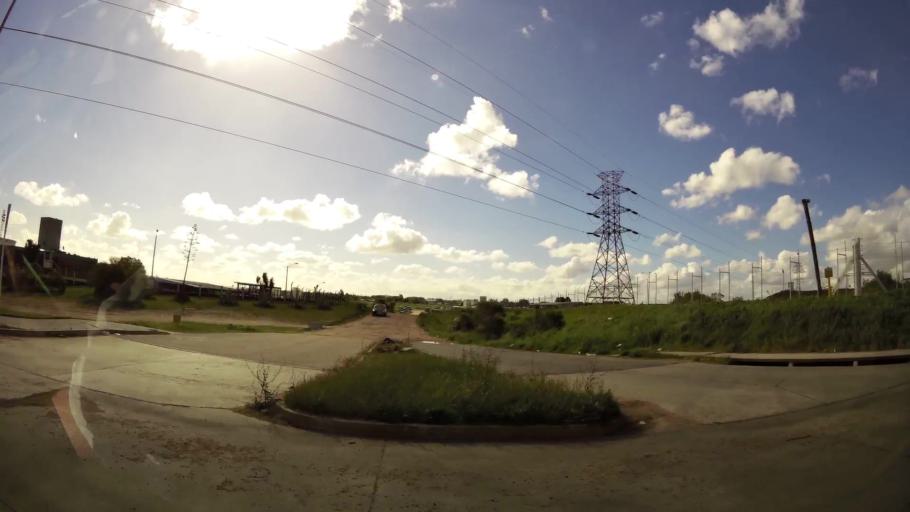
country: UY
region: Canelones
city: La Paz
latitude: -34.8183
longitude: -56.2359
